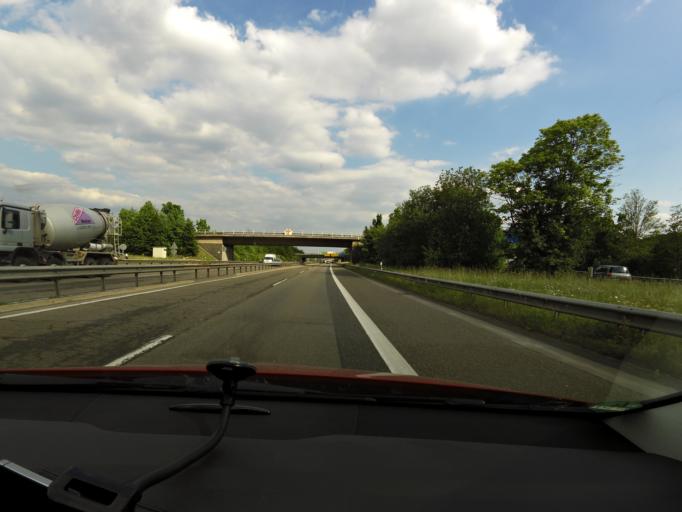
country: DE
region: Rheinland-Pfalz
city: Kaltenengers
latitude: 50.3947
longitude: 7.5410
